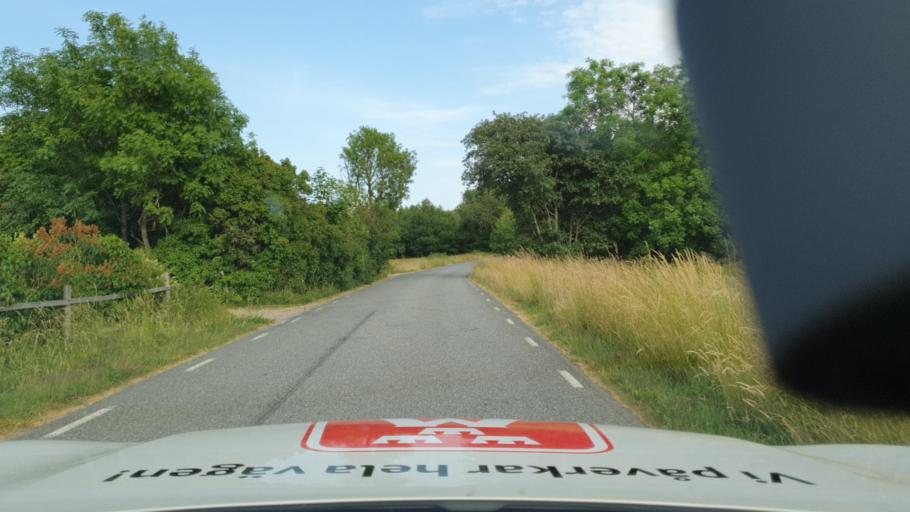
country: SE
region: Skane
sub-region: Kristianstads Kommun
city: Degeberga
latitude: 55.6895
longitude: 14.0925
